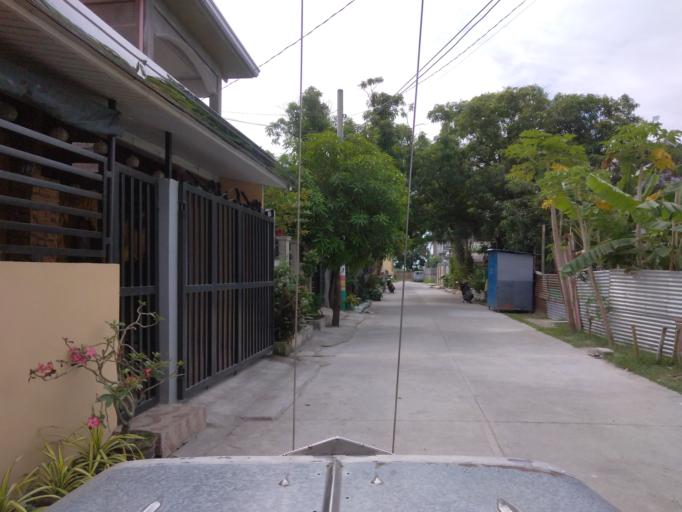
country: PH
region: Central Luzon
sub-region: Province of Pampanga
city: Sexmoan
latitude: 14.9443
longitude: 120.6213
